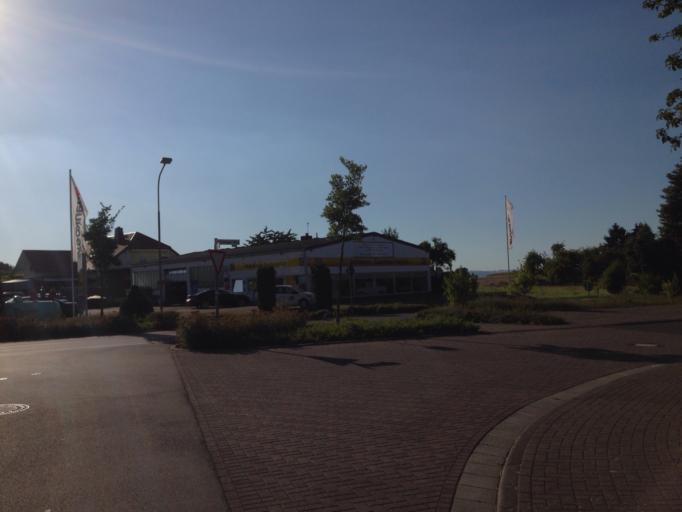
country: DE
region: Hesse
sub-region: Regierungsbezirk Giessen
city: Lich
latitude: 50.5339
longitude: 8.7478
